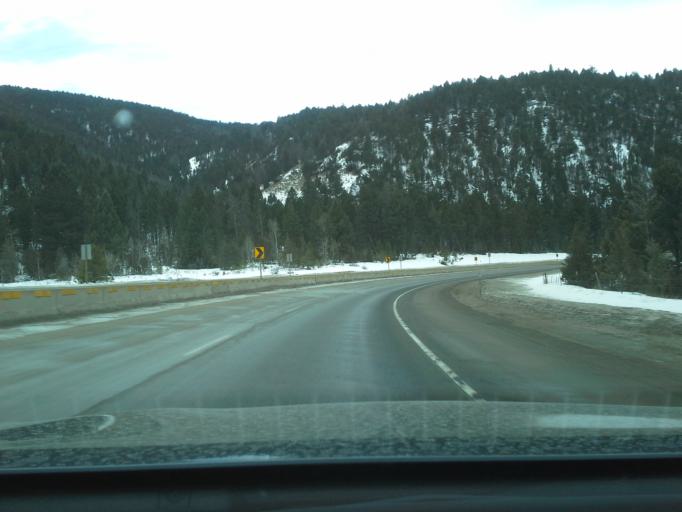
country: US
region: Montana
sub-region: Jefferson County
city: Boulder
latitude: 46.2580
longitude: -112.2128
